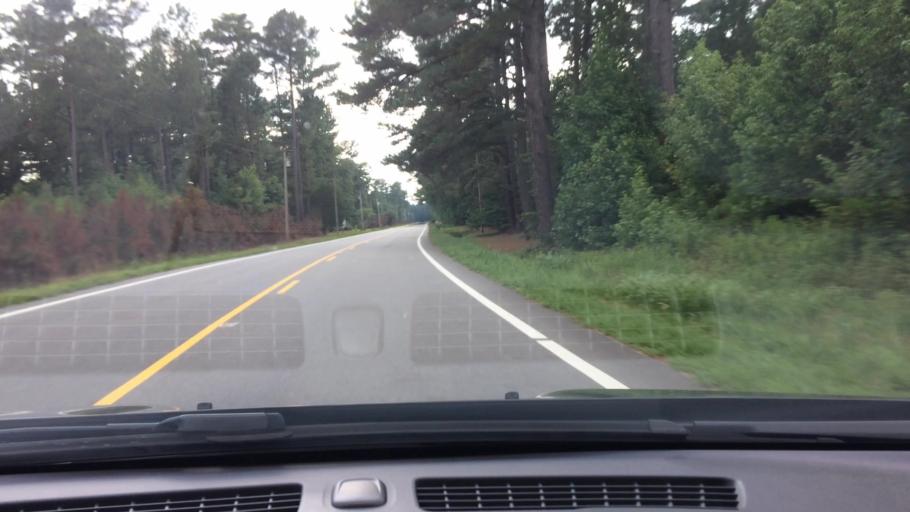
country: US
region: North Carolina
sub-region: Craven County
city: Vanceboro
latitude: 35.4177
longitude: -77.2401
